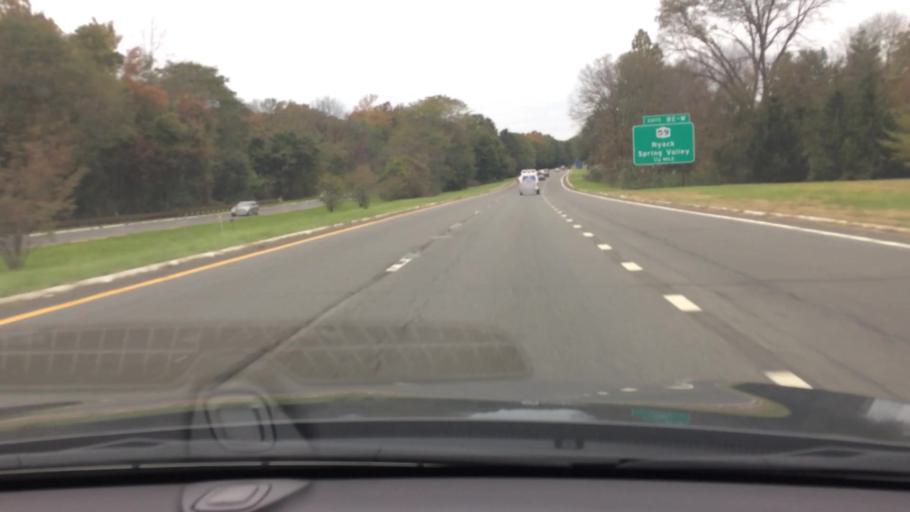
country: US
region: New York
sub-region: Rockland County
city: West Nyack
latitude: 41.0815
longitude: -73.9868
